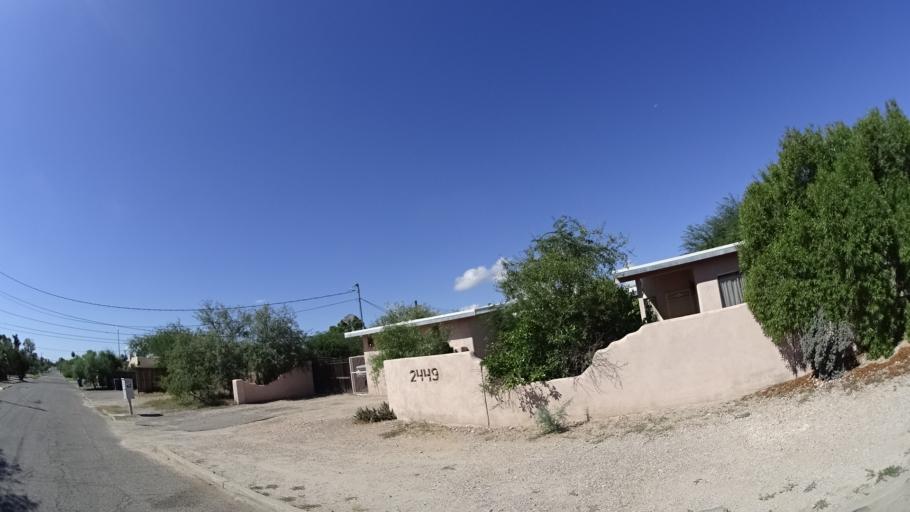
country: US
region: Arizona
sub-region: Pima County
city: Tucson
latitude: 32.2508
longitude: -110.9539
